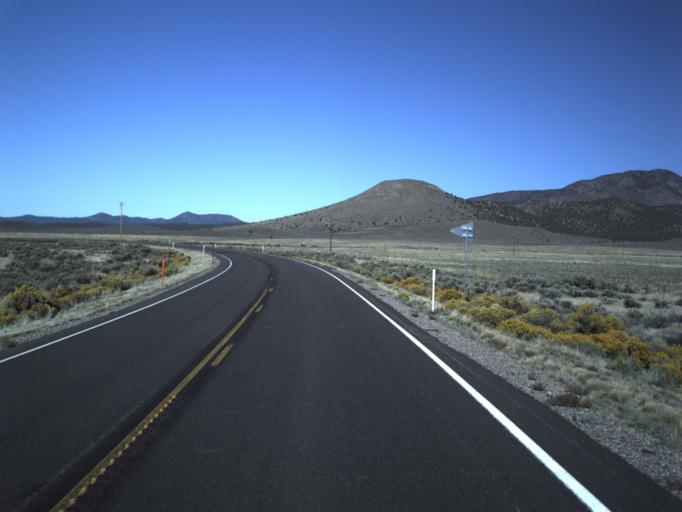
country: US
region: Utah
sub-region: Washington County
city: Enterprise
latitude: 37.8027
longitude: -113.9205
